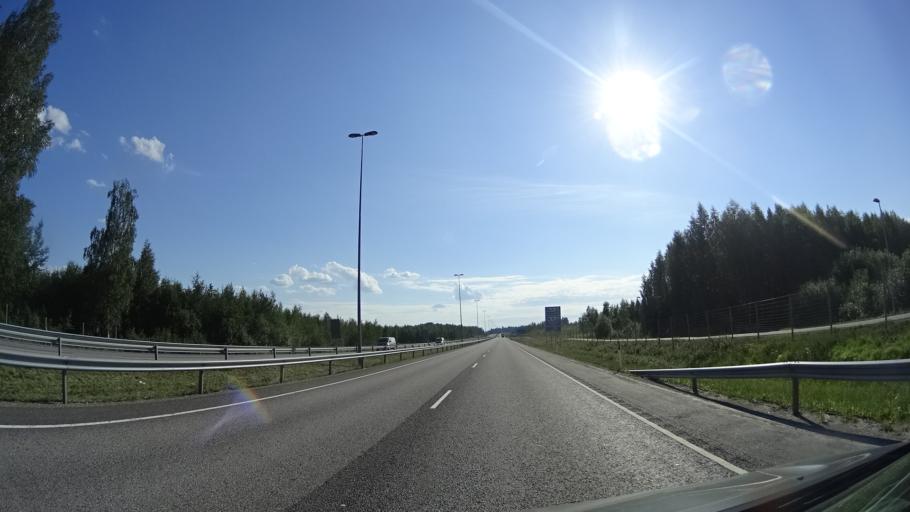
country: FI
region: South Karelia
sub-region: Imatra
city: Imatra
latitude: 61.1812
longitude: 28.7288
